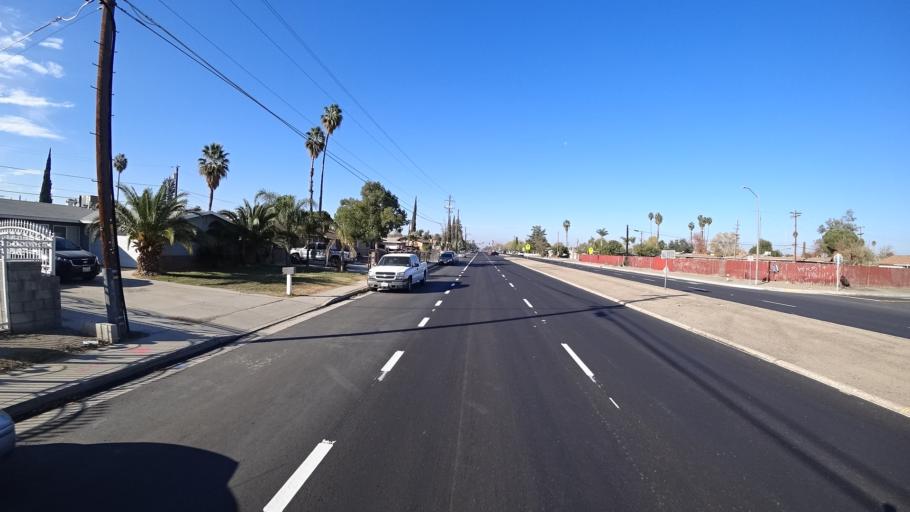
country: US
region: California
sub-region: Kern County
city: Greenfield
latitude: 35.3176
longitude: -119.0088
